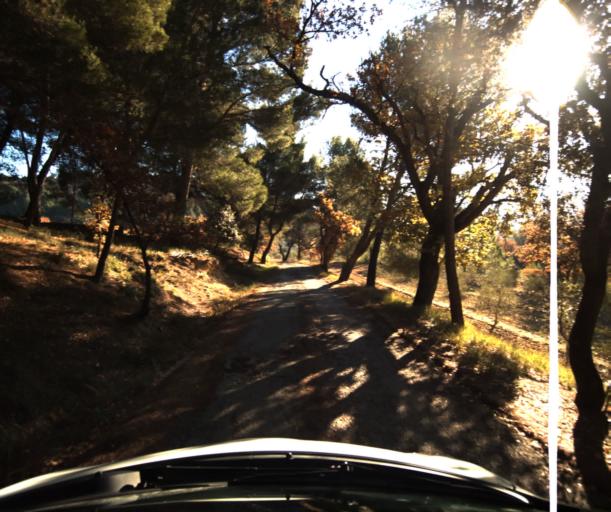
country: FR
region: Provence-Alpes-Cote d'Azur
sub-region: Departement du Vaucluse
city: Pertuis
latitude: 43.7172
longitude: 5.4931
